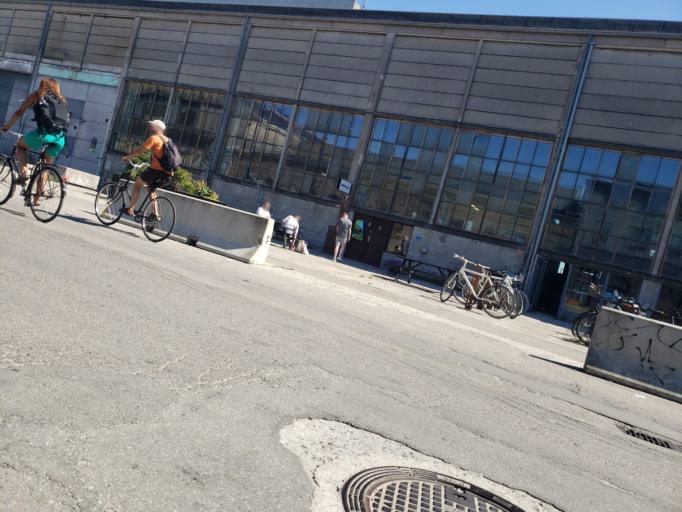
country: DK
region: Capital Region
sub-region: Kobenhavn
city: Christianshavn
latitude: 55.6921
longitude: 12.6126
